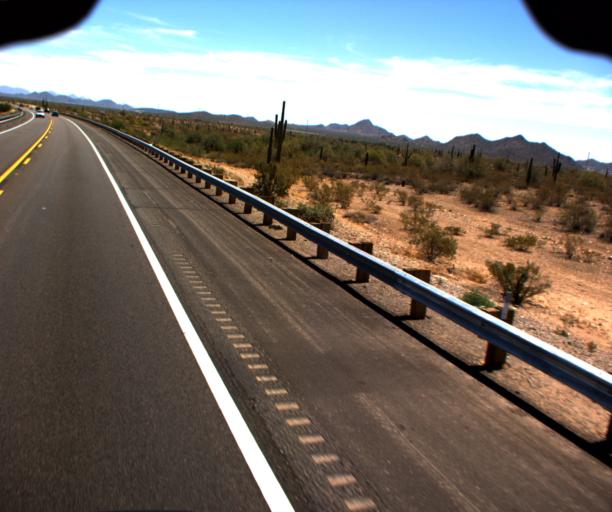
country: US
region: Arizona
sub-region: Maricopa County
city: Anthem
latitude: 33.7996
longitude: -112.2335
